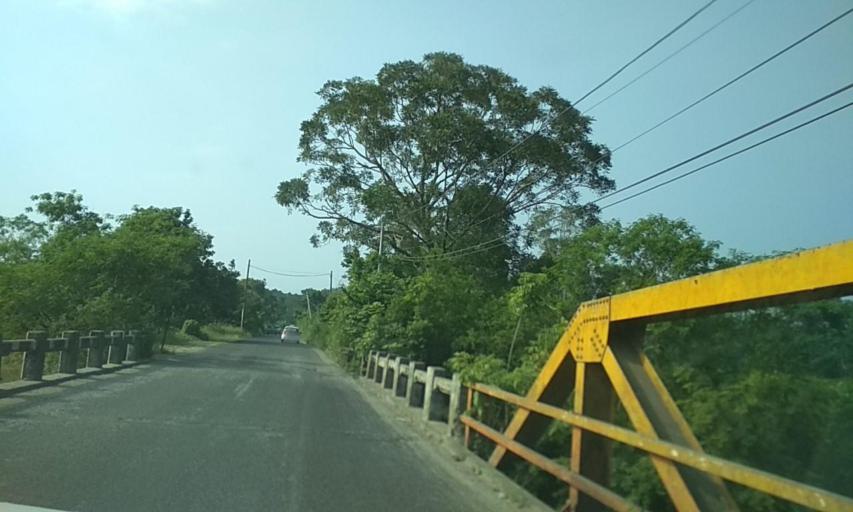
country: MX
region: Veracruz
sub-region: Misantla
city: La Defensa
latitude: 20.0524
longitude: -96.9790
